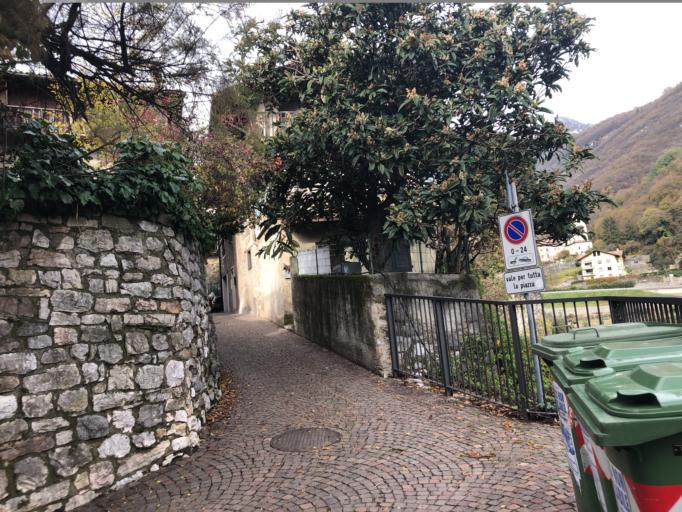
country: IT
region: Trentino-Alto Adige
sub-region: Provincia di Trento
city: Tenno
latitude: 45.9153
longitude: 10.8342
